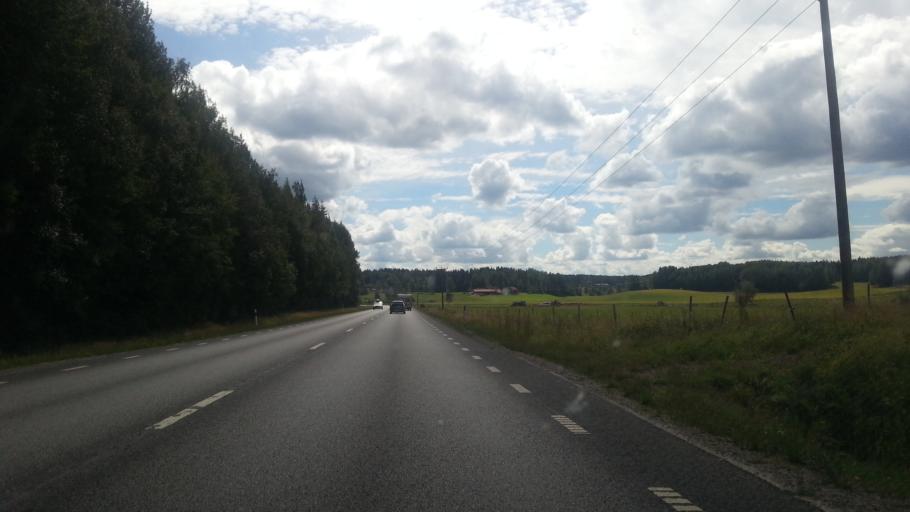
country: SE
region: OErebro
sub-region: Lindesbergs Kommun
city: Lindesberg
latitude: 59.5756
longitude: 15.2049
